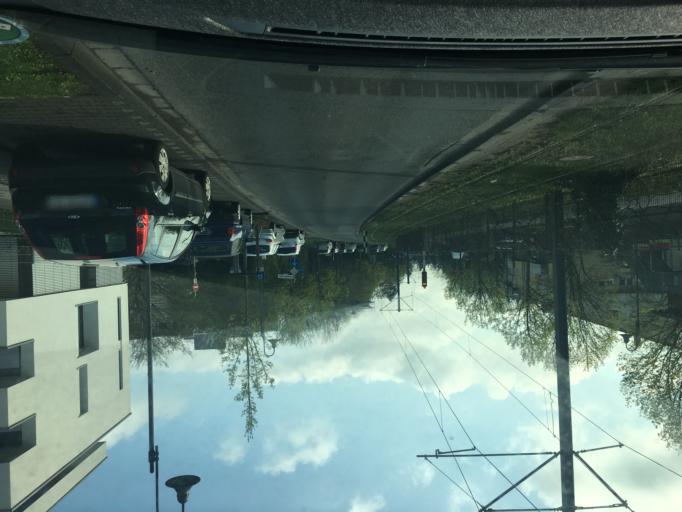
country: DE
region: North Rhine-Westphalia
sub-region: Regierungsbezirk Koln
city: Bonn
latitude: 50.7564
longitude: 7.0751
